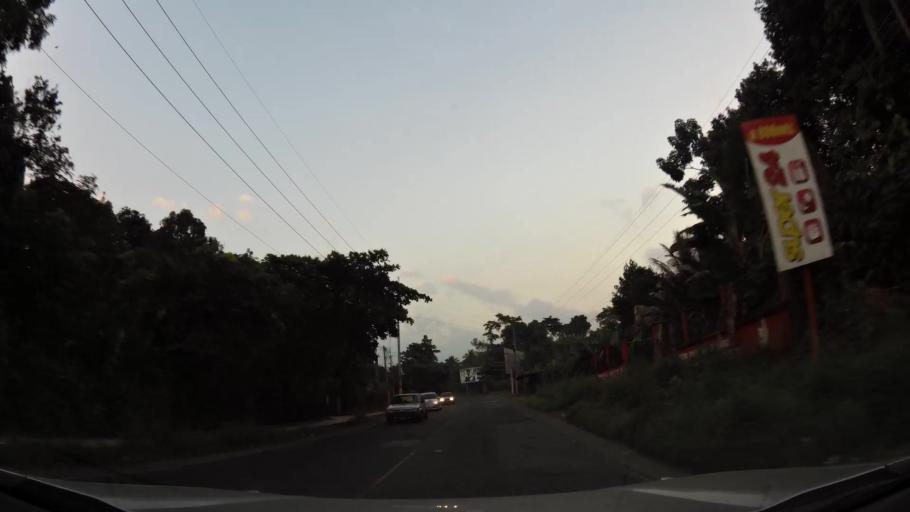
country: GT
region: Retalhuleu
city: Santa Cruz Mulua
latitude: 14.5899
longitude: -91.6206
